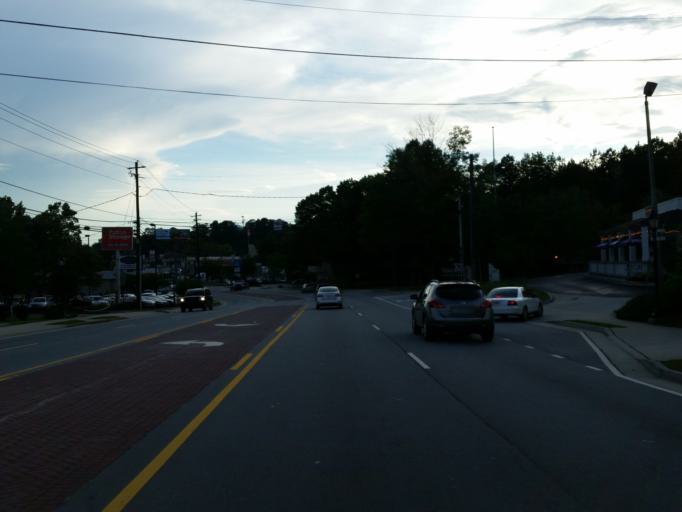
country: US
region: Georgia
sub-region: Fulton County
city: Roswell
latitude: 34.0344
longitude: -84.3474
